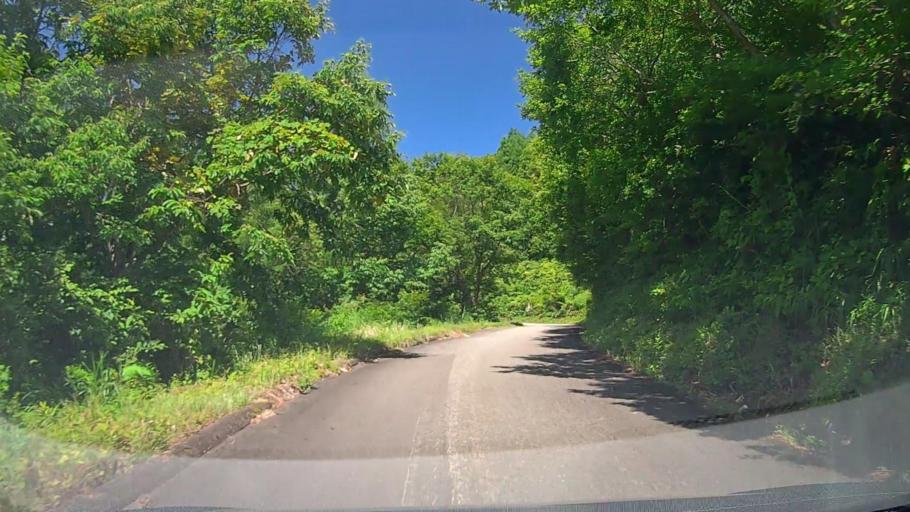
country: JP
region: Nagano
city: Iiyama
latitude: 36.9327
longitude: 138.4570
